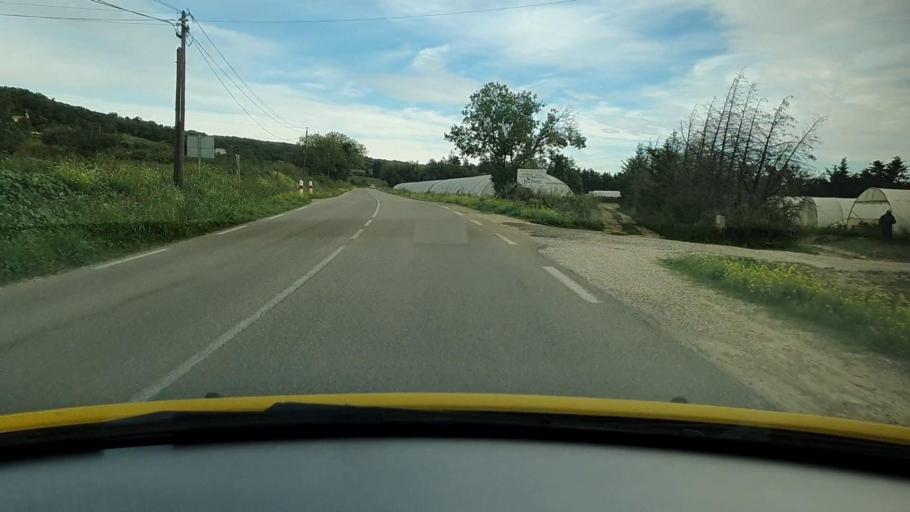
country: FR
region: Languedoc-Roussillon
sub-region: Departement du Gard
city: Bellegarde
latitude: 43.7676
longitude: 4.5321
